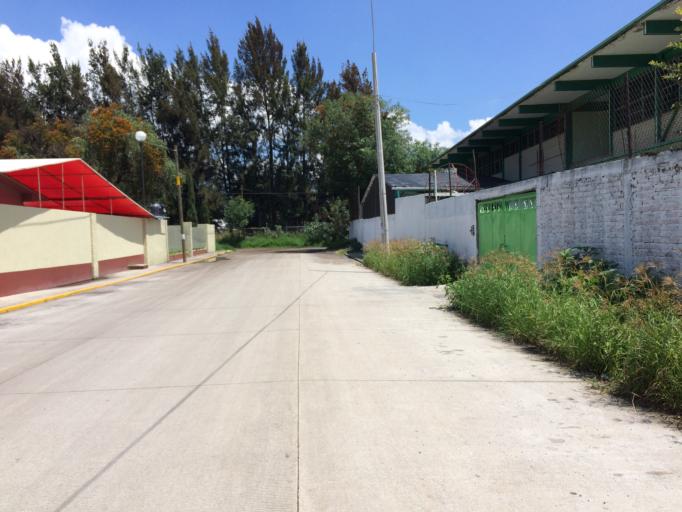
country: MX
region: Michoacan
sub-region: Morelia
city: Morelos
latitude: 19.6838
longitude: -101.2342
